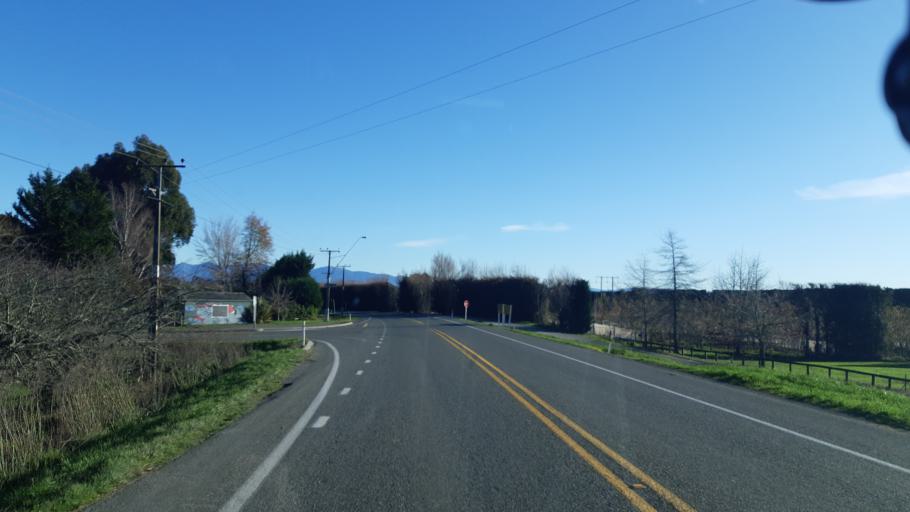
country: NZ
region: Tasman
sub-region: Tasman District
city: Richmond
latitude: -41.3090
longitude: 173.1273
